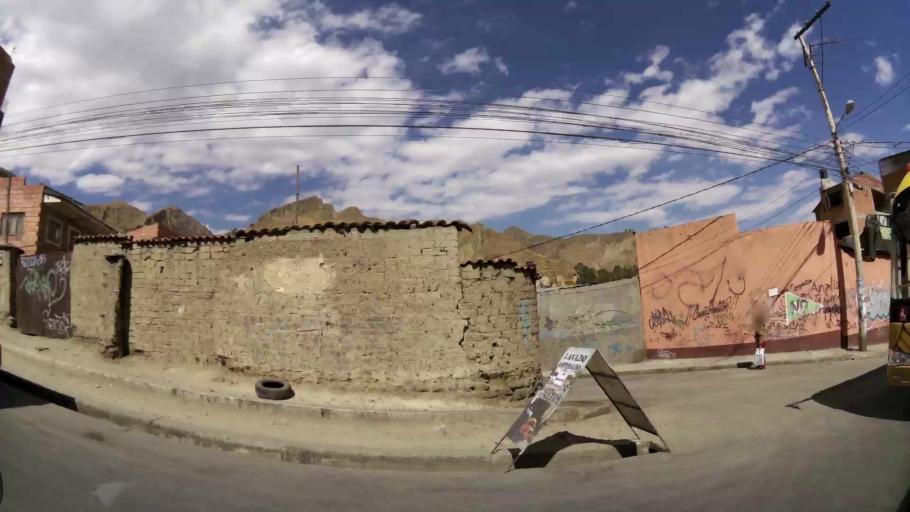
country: BO
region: La Paz
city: La Paz
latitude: -16.4663
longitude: -68.1111
